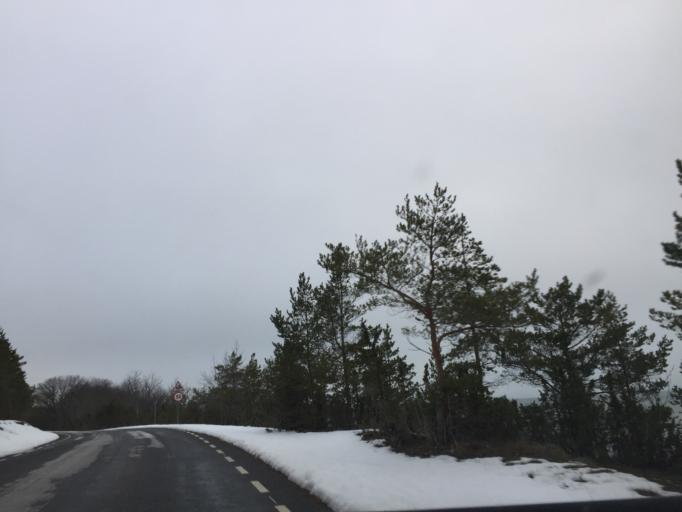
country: EE
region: Saare
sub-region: Kuressaare linn
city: Kuressaare
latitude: 58.5666
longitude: 22.3062
